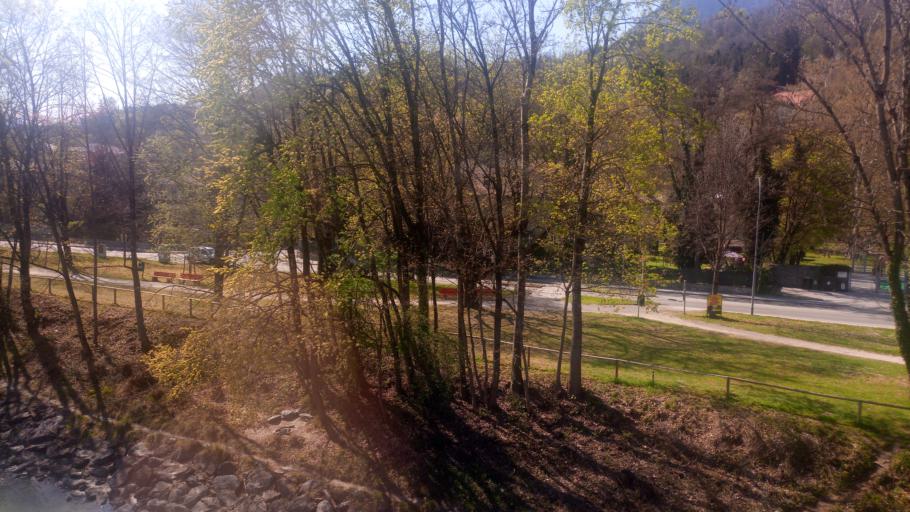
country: AT
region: Tyrol
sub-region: Innsbruck Stadt
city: Innsbruck
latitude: 47.2789
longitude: 11.3998
